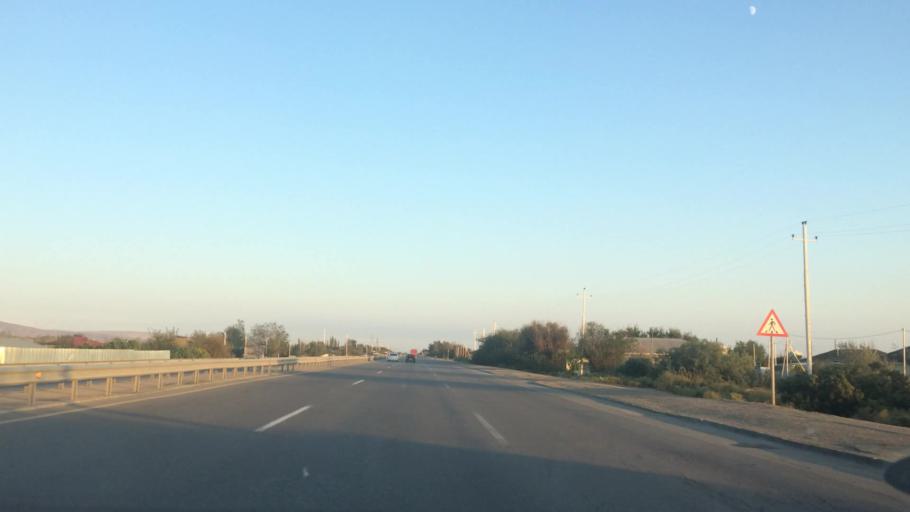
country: AZ
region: Haciqabul
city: Haciqabul
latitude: 40.0190
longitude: 49.1324
